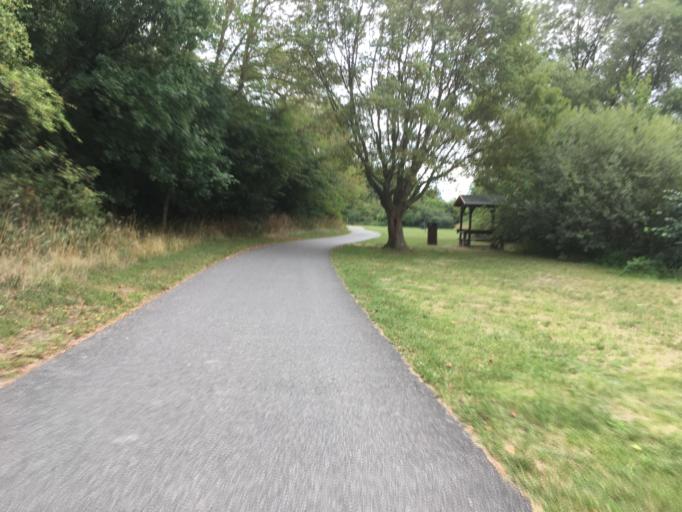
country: DE
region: Brandenburg
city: Prenzlau
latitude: 53.2935
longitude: 13.8685
